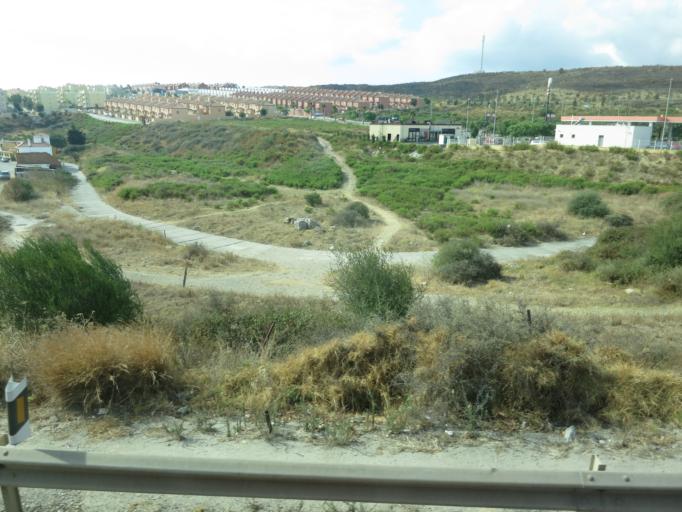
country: ES
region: Andalusia
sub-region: Provincia de Cadiz
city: Algeciras
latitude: 36.1132
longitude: -5.4526
